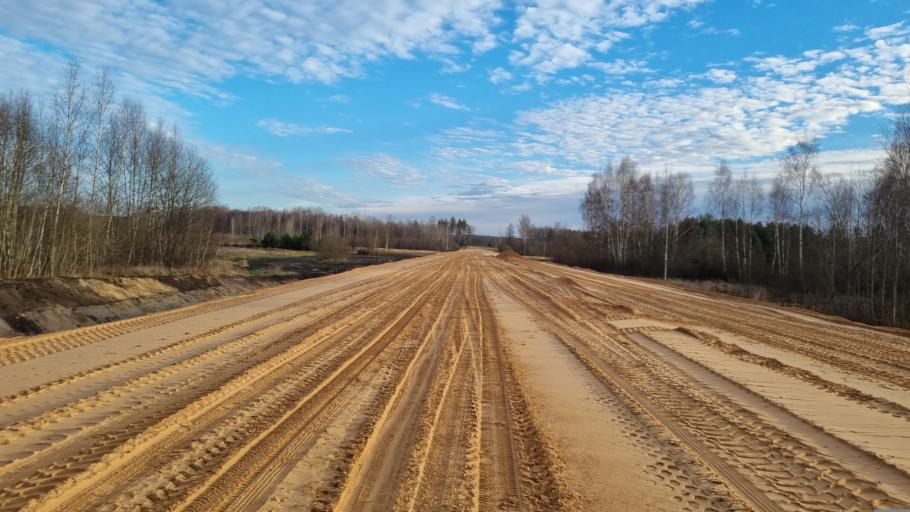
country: LV
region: Kekava
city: Kekava
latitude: 56.7852
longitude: 24.2271
